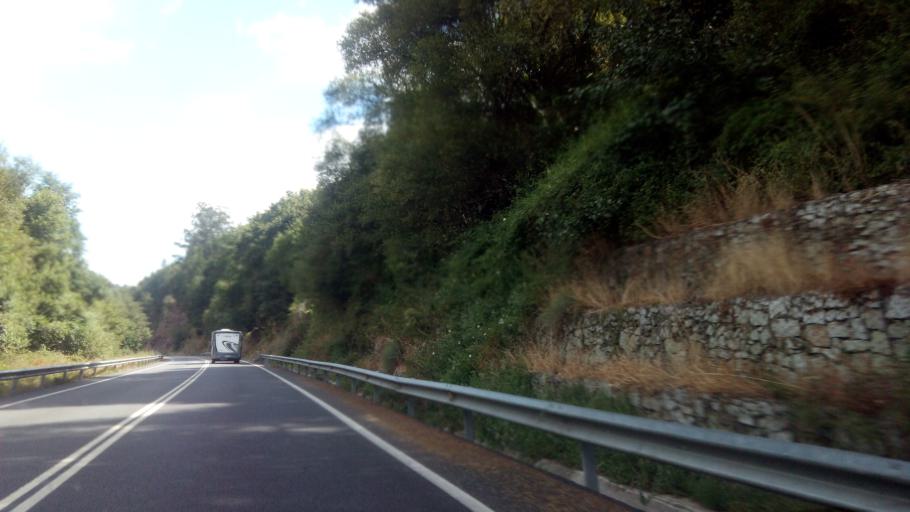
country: ES
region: Galicia
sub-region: Provincia de Ourense
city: Nogueira de Ramuin
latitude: 42.4319
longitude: -7.7526
